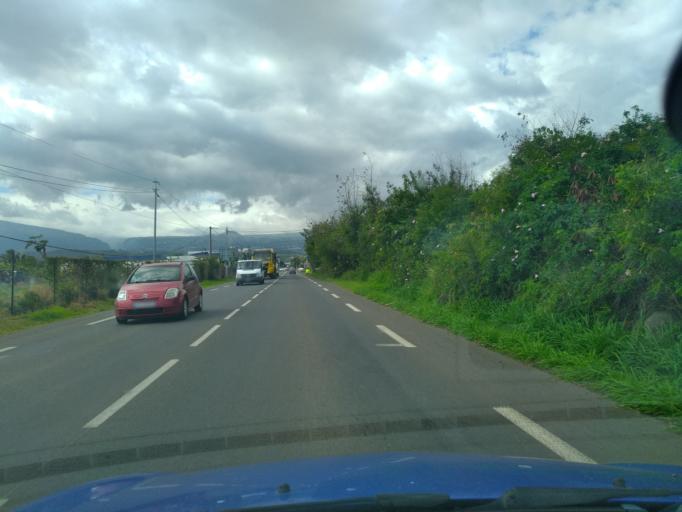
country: RE
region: Reunion
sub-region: Reunion
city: Saint-Louis
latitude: -21.2985
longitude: 55.4380
